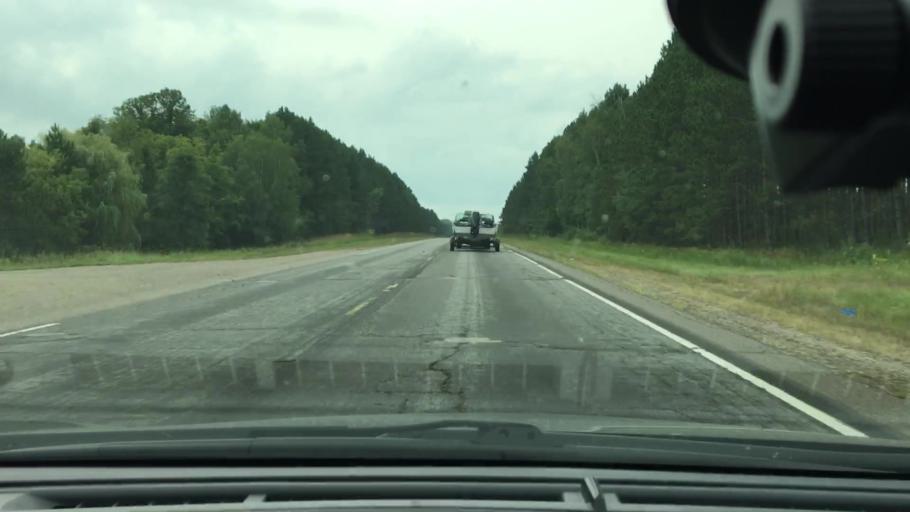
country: US
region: Minnesota
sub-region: Crow Wing County
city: Crosby
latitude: 46.6370
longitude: -93.9493
